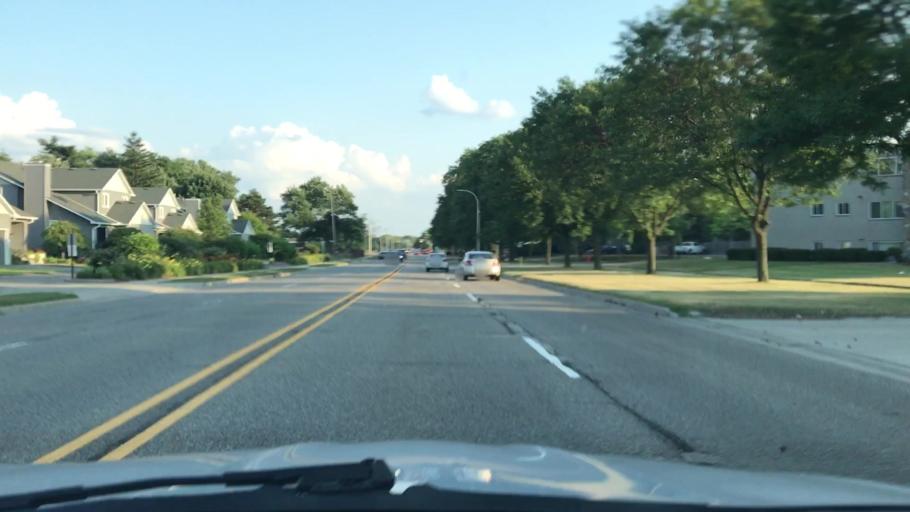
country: US
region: Michigan
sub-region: Oakland County
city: Clawson
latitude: 42.5288
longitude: -83.1653
